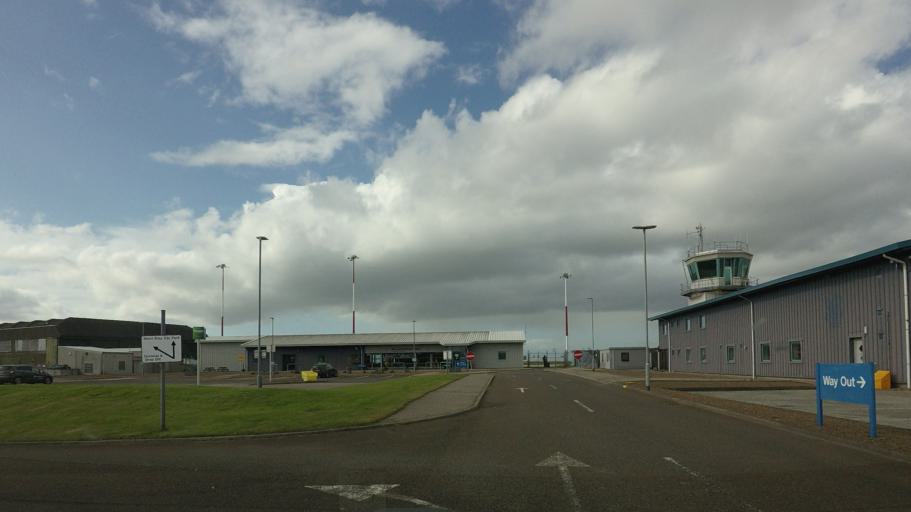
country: GB
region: Scotland
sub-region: Highland
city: Wick
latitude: 58.4531
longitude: -3.0865
